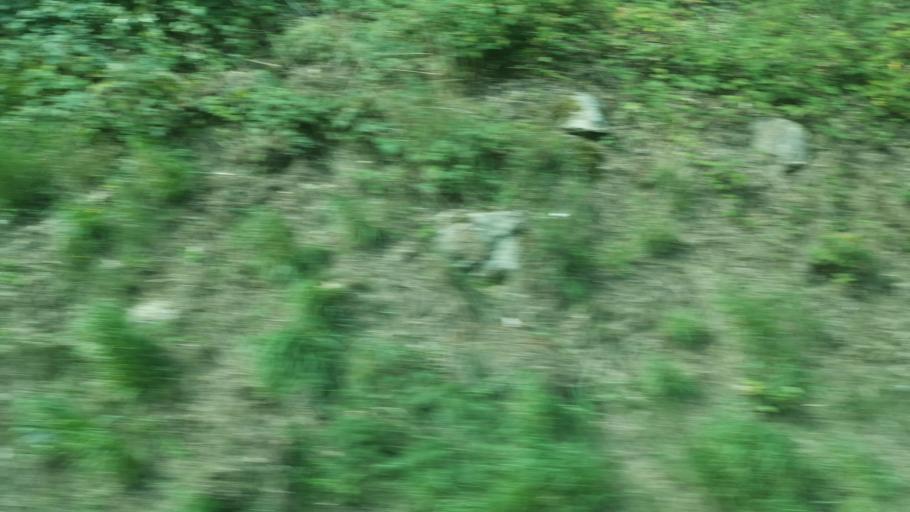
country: DE
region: Bavaria
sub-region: Upper Palatinate
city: Chamerau
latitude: 49.1889
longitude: 12.7323
